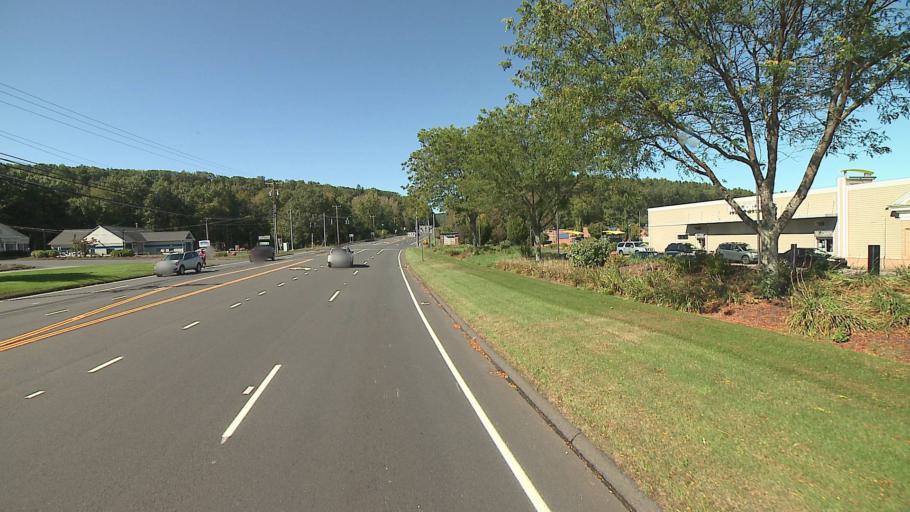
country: US
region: Connecticut
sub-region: Hartford County
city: Canton Valley
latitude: 41.8175
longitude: -72.8685
